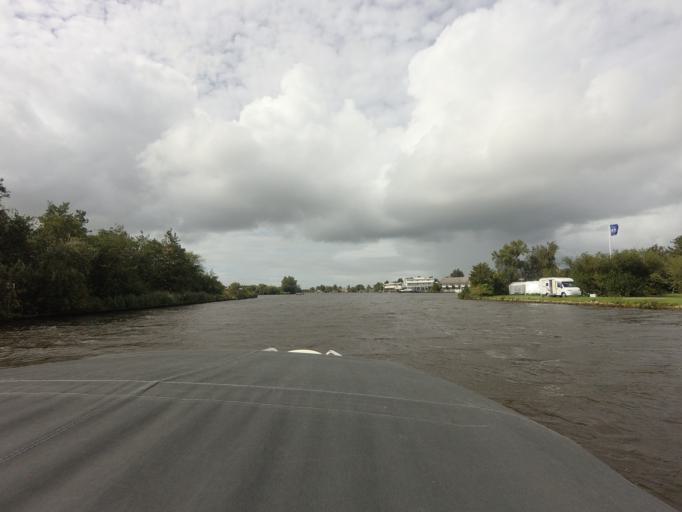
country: NL
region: Friesland
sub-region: Gemeente Boarnsterhim
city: Warten
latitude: 53.1265
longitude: 5.9362
